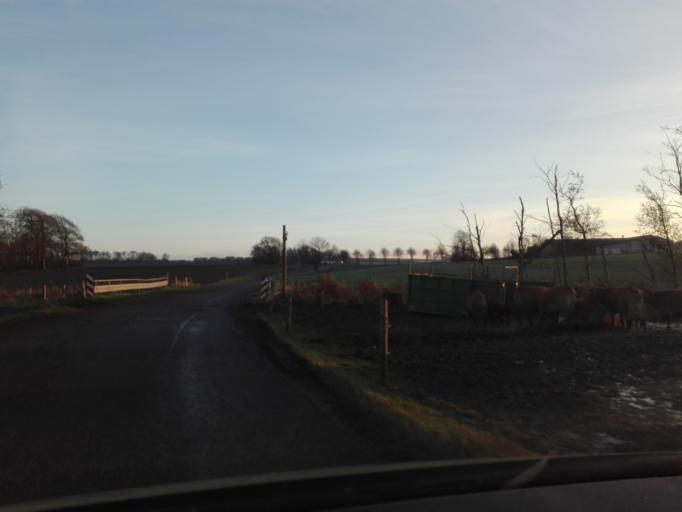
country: DK
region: Central Jutland
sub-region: Skanderborg Kommune
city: Galten
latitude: 56.1683
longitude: 9.9289
